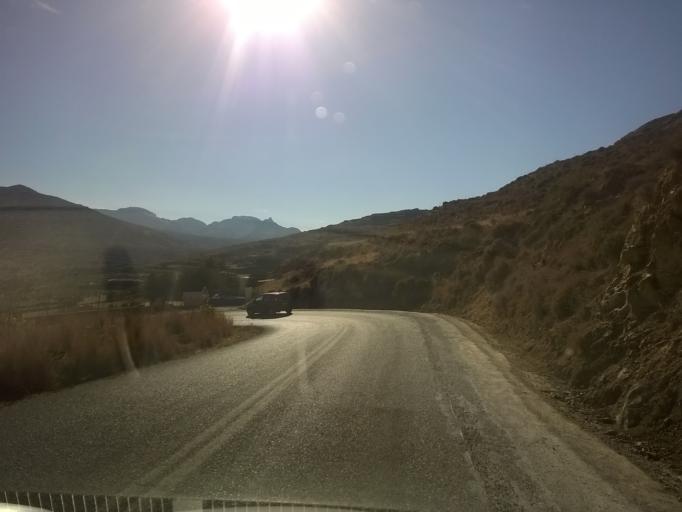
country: GR
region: South Aegean
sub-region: Nomos Kykladon
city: Naxos
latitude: 37.1140
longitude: 25.4219
